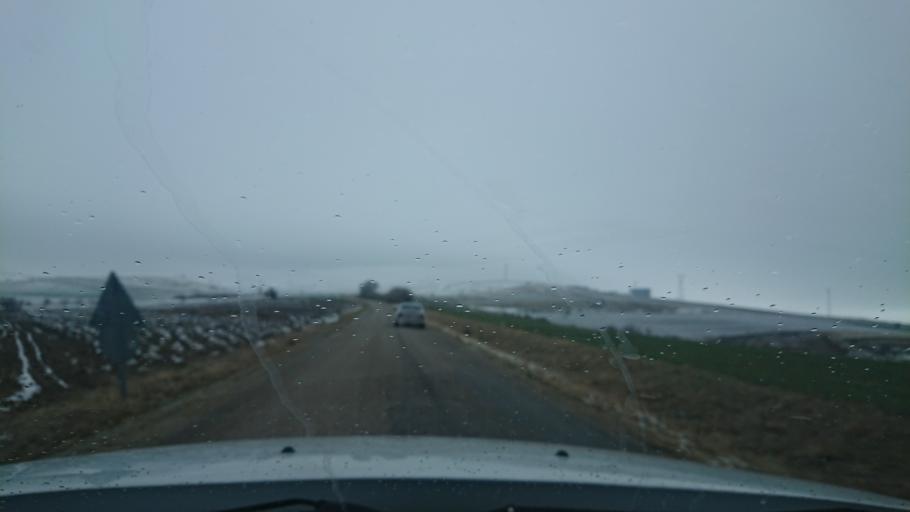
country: TR
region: Aksaray
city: Agacoren
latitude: 38.8531
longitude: 33.9513
